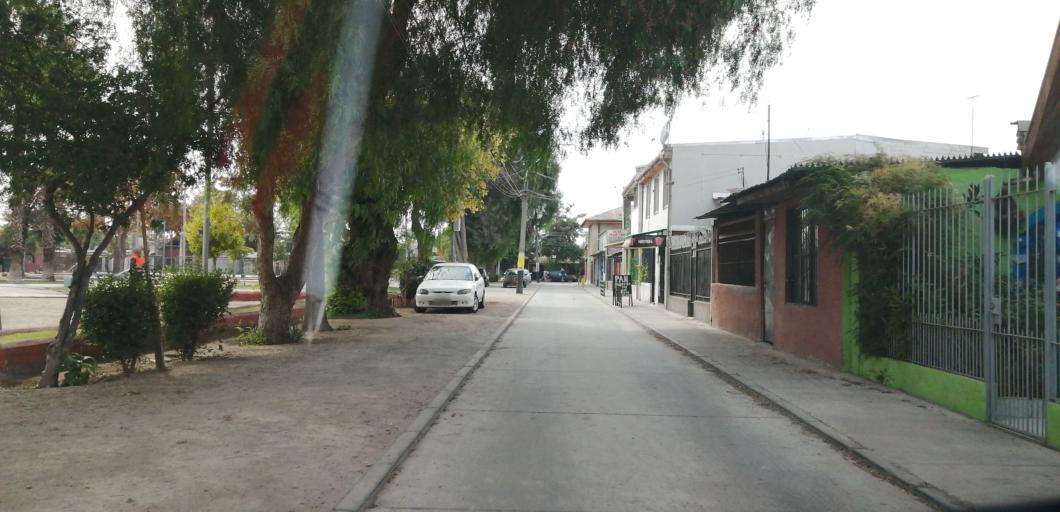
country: CL
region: Santiago Metropolitan
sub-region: Provincia de Santiago
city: Lo Prado
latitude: -33.4341
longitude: -70.7486
